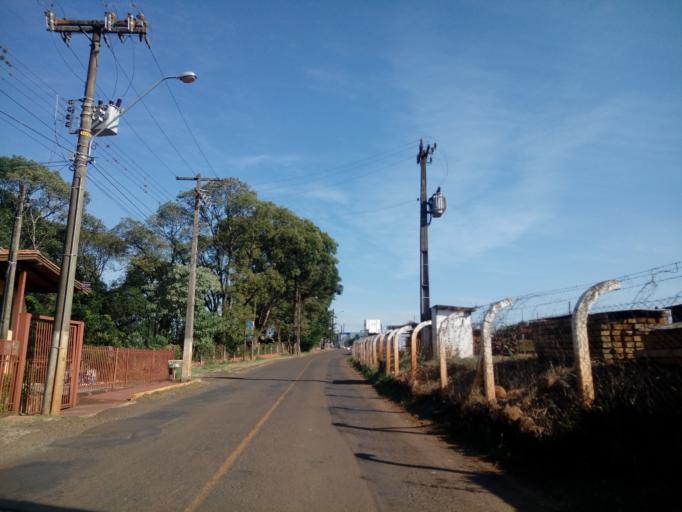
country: BR
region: Santa Catarina
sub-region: Chapeco
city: Chapeco
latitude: -27.0947
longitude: -52.6640
